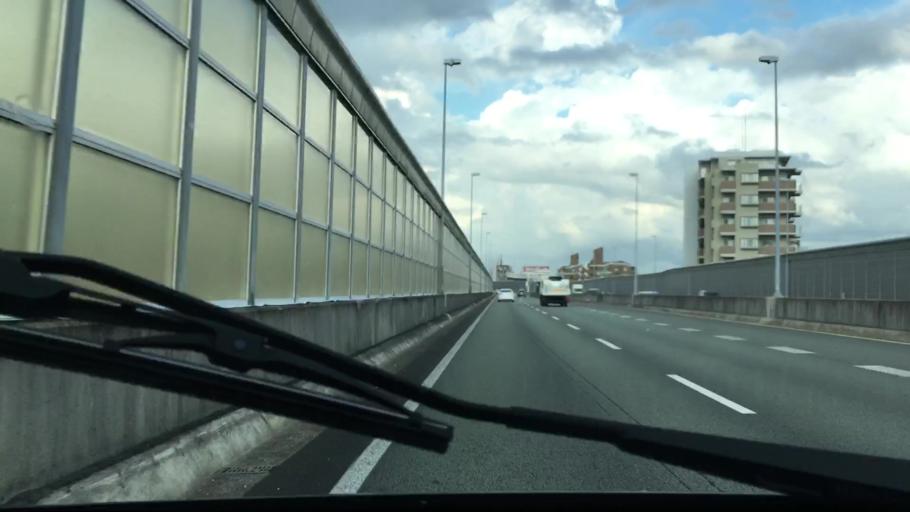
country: JP
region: Fukuoka
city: Fukuoka-shi
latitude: 33.5803
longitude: 130.3325
